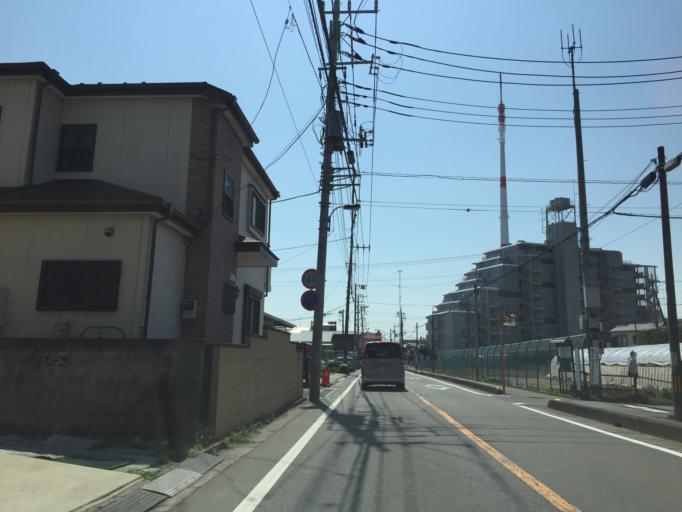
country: JP
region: Saitama
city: Yono
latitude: 35.8558
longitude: 139.6152
